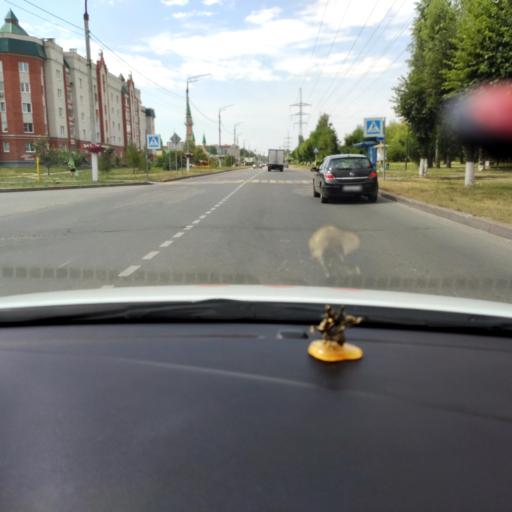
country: RU
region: Tatarstan
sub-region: Zelenodol'skiy Rayon
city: Zelenodolsk
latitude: 55.8532
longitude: 48.5061
